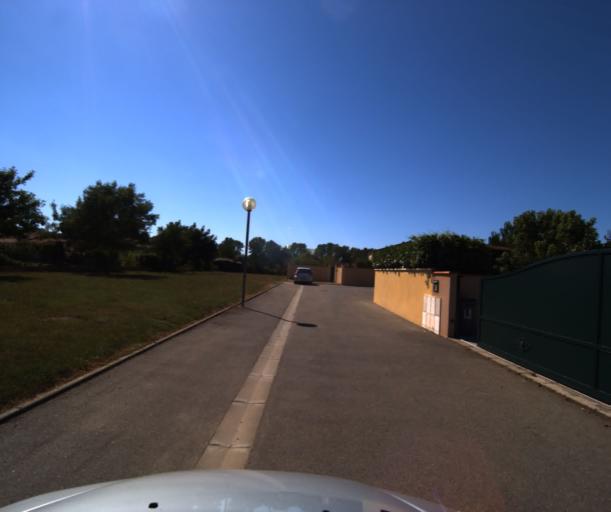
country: FR
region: Midi-Pyrenees
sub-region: Departement de la Haute-Garonne
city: Le Fauga
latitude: 43.4230
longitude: 1.3171
